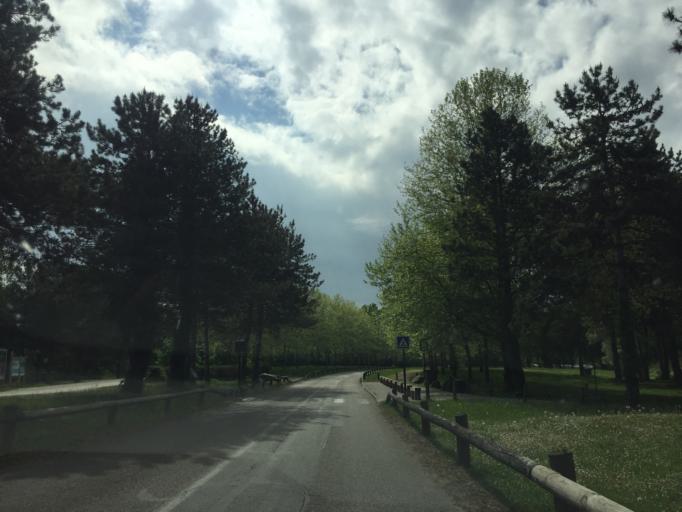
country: FR
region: Rhone-Alpes
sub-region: Departement du Rhone
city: Vaulx-en-Velin
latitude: 45.8020
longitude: 4.9355
